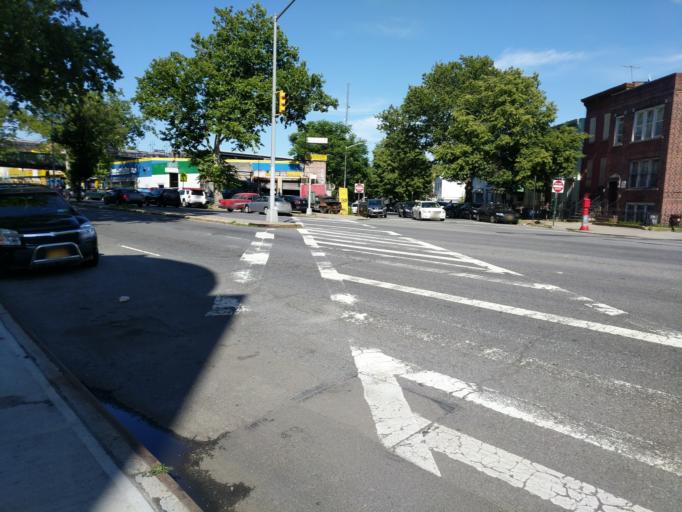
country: US
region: New York
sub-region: Kings County
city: East New York
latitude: 40.6793
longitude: -73.9065
